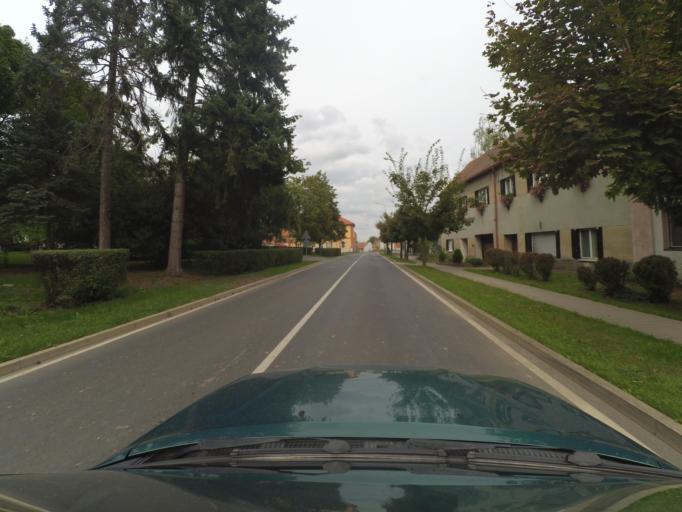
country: CZ
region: Central Bohemia
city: Revnicov
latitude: 50.2530
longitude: 13.7737
